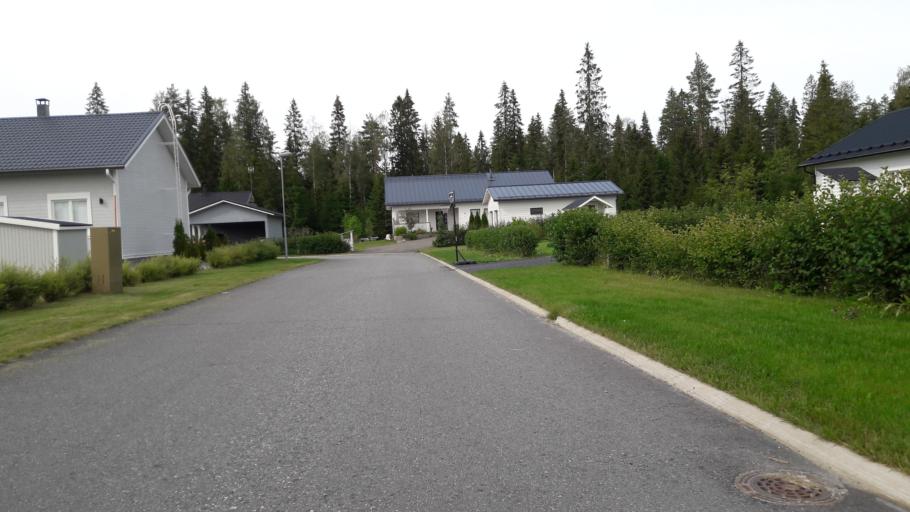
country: FI
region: North Karelia
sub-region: Joensuu
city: Joensuu
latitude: 62.5732
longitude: 29.8252
